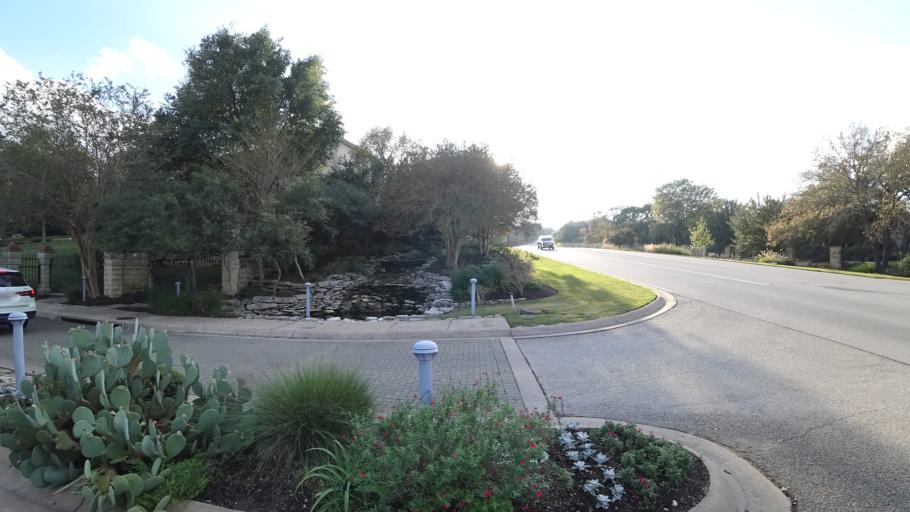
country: US
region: Texas
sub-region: Travis County
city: Lost Creek
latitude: 30.2966
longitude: -97.8576
